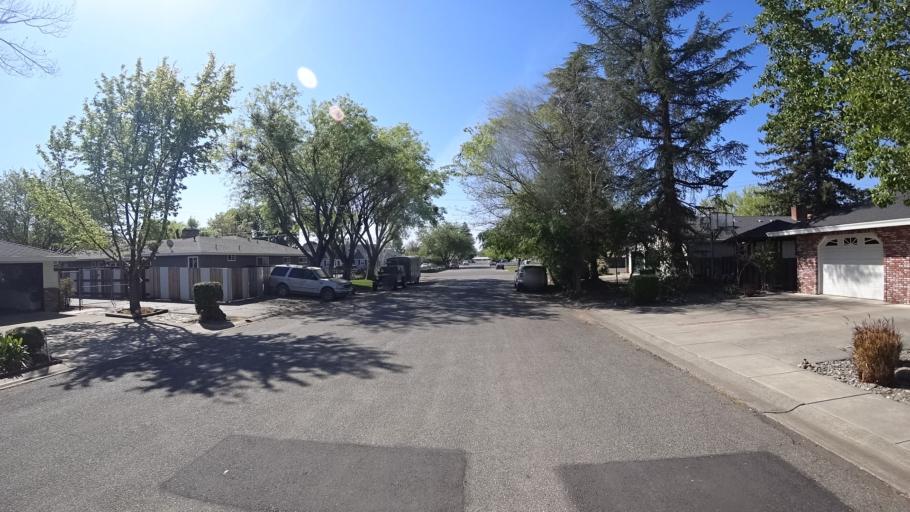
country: US
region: California
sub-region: Glenn County
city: Willows
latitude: 39.5272
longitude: -122.2057
